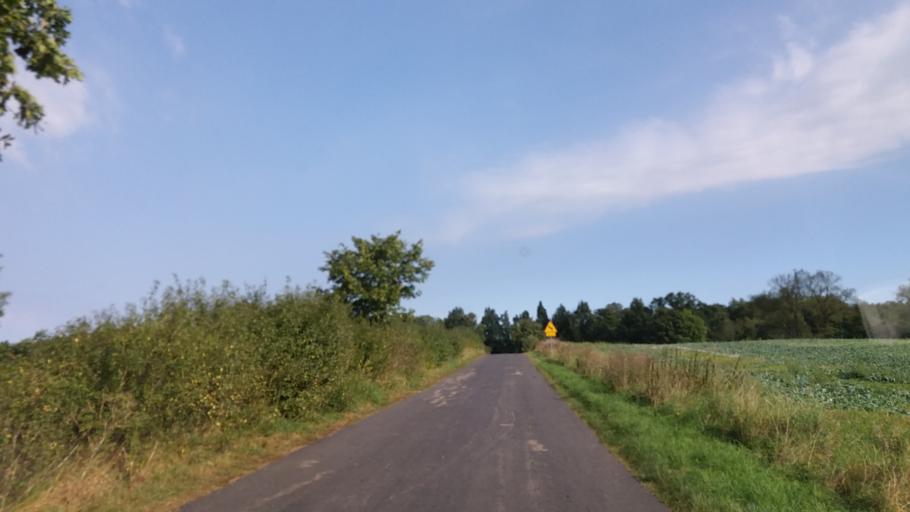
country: PL
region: West Pomeranian Voivodeship
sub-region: Powiat stargardzki
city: Suchan
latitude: 53.2211
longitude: 15.3415
